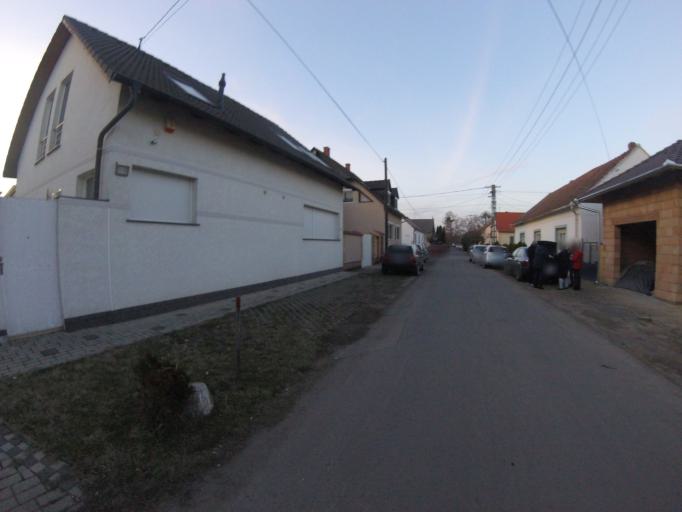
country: HU
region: Baranya
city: Mohacs
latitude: 45.9980
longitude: 18.6763
